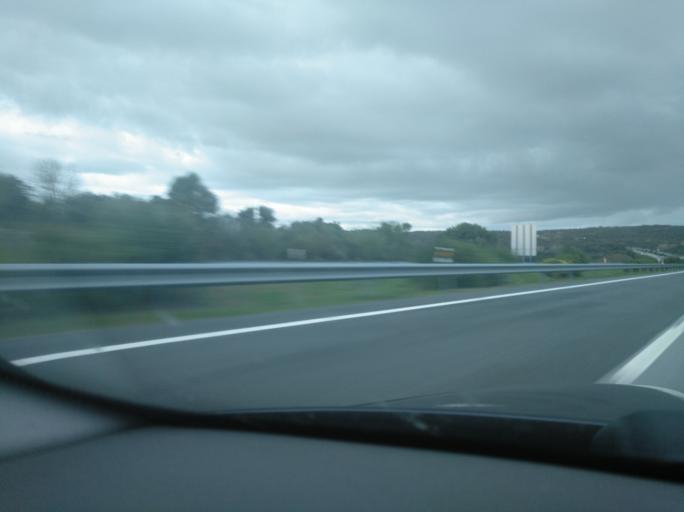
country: PT
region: Evora
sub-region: Evora
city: Evora
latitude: 38.6037
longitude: -8.0143
